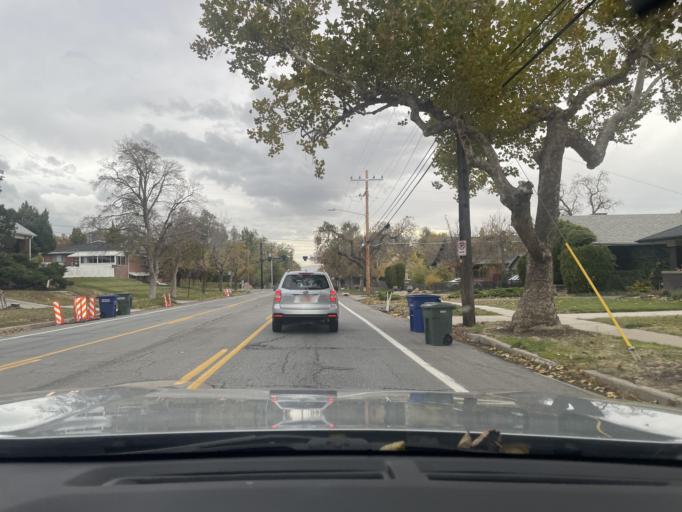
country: US
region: Utah
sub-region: Salt Lake County
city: Salt Lake City
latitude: 40.7467
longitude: -111.8539
